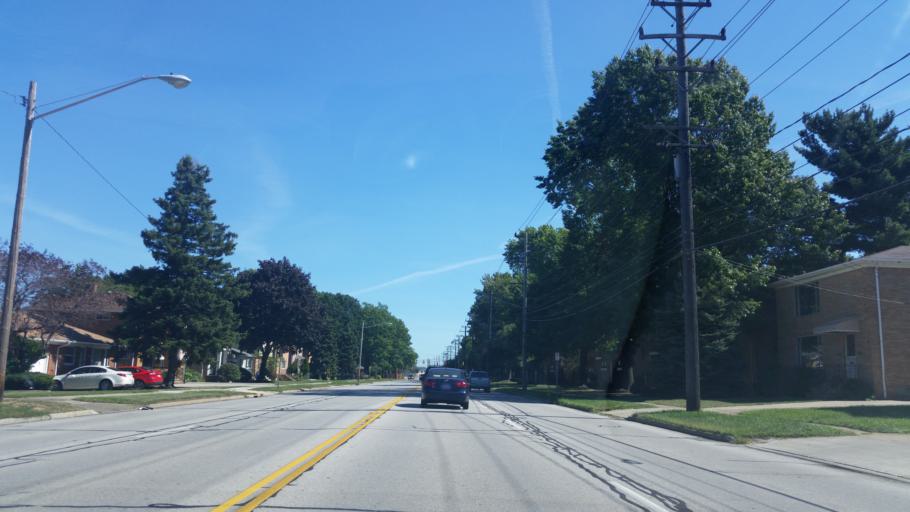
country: US
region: Ohio
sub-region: Cuyahoga County
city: Parma
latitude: 41.4050
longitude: -81.7029
